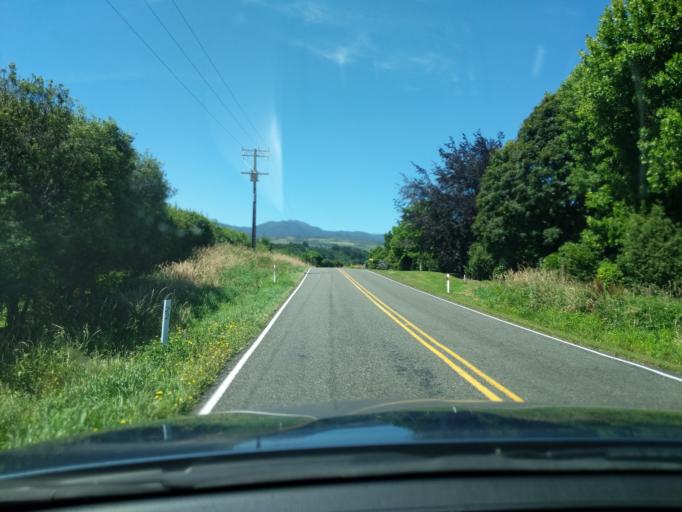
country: NZ
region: Tasman
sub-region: Tasman District
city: Takaka
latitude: -40.7137
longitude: 172.6379
